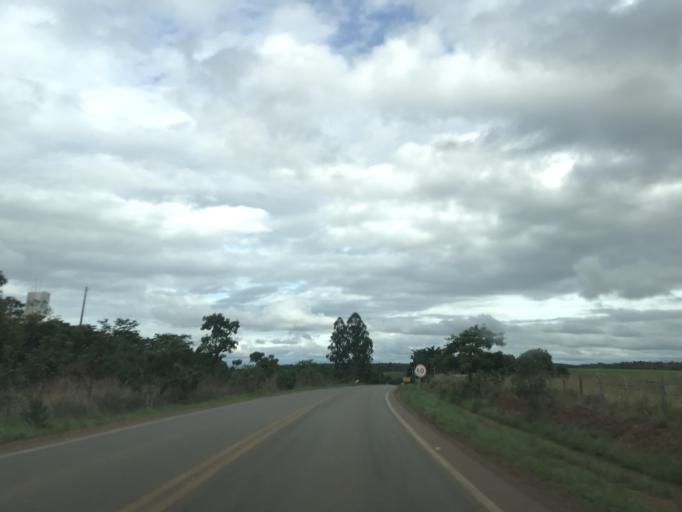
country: BR
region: Goias
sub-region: Vianopolis
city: Vianopolis
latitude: -16.7260
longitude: -48.4375
